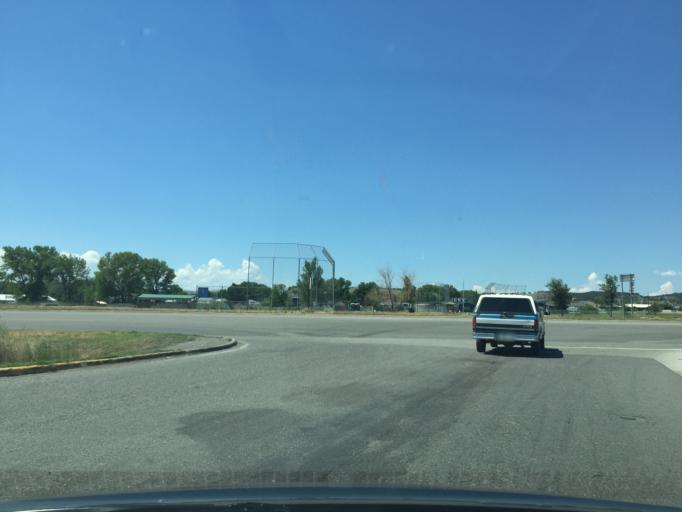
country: US
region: Montana
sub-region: Stillwater County
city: Columbus
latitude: 45.6446
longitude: -109.2482
